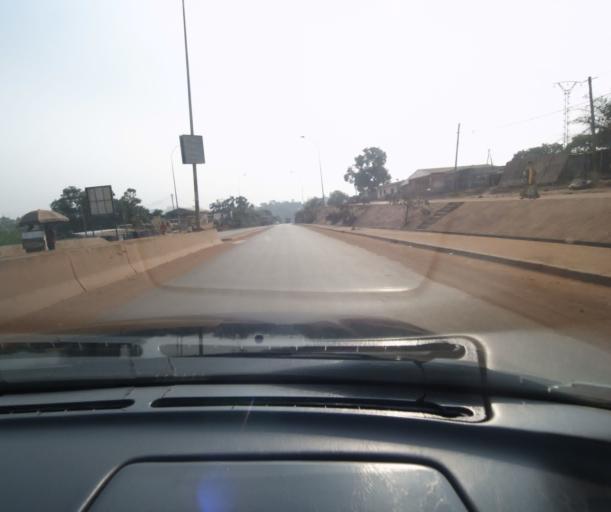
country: CM
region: Centre
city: Okoa
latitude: 3.9575
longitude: 11.5347
